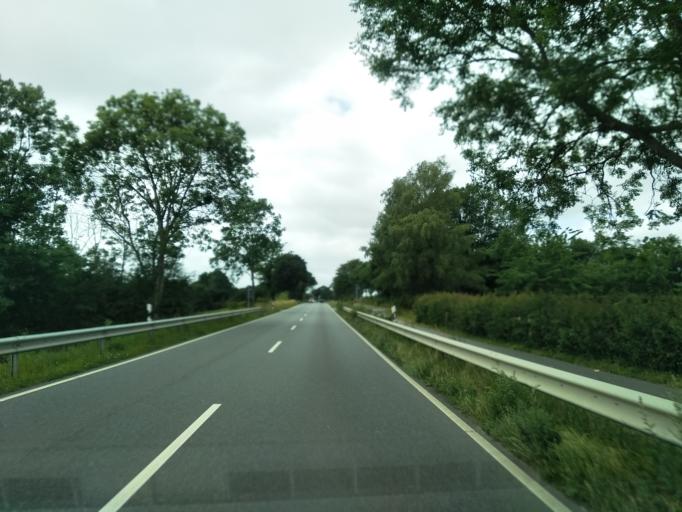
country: DE
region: Schleswig-Holstein
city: Langballig
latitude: 54.7988
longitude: 9.6264
